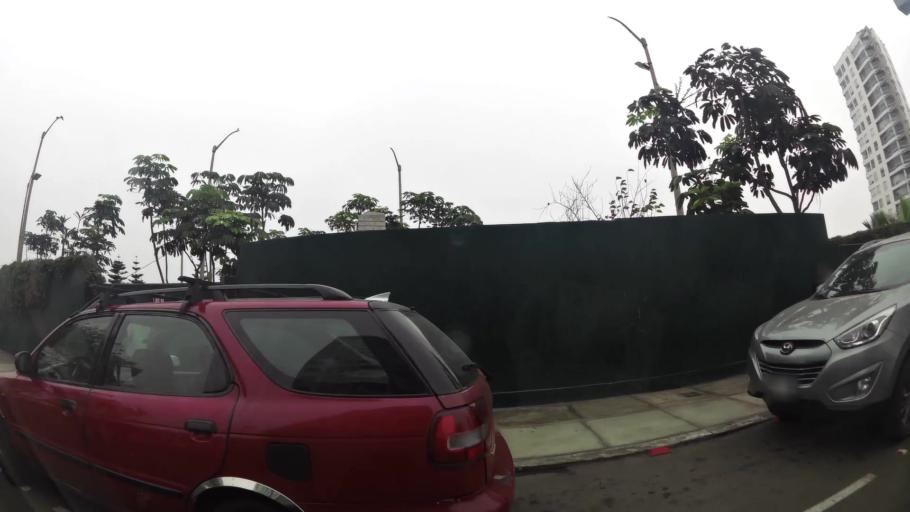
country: PE
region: Lima
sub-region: Lima
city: San Isidro
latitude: -12.1175
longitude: -77.0458
